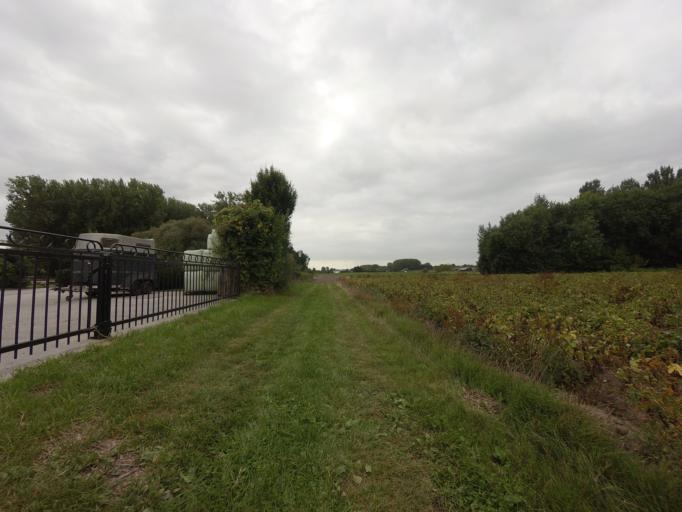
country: BE
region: Flanders
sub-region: Provincie Vlaams-Brabant
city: Kapelle-op-den-Bos
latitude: 50.9761
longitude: 4.3425
